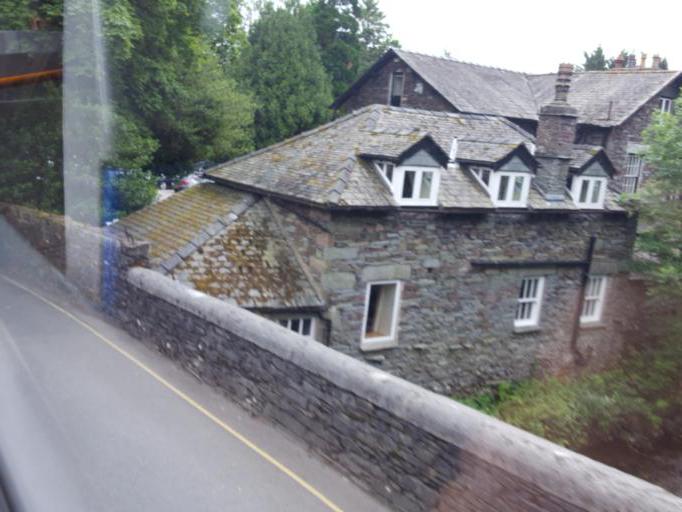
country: GB
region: England
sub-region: Cumbria
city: Ambleside
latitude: 54.4572
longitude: -3.0237
